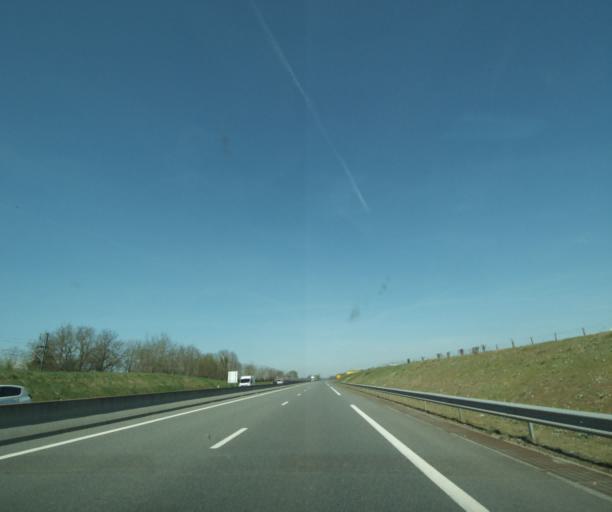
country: FR
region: Auvergne
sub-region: Departement de l'Allier
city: Trevol
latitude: 46.6091
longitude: 3.2941
